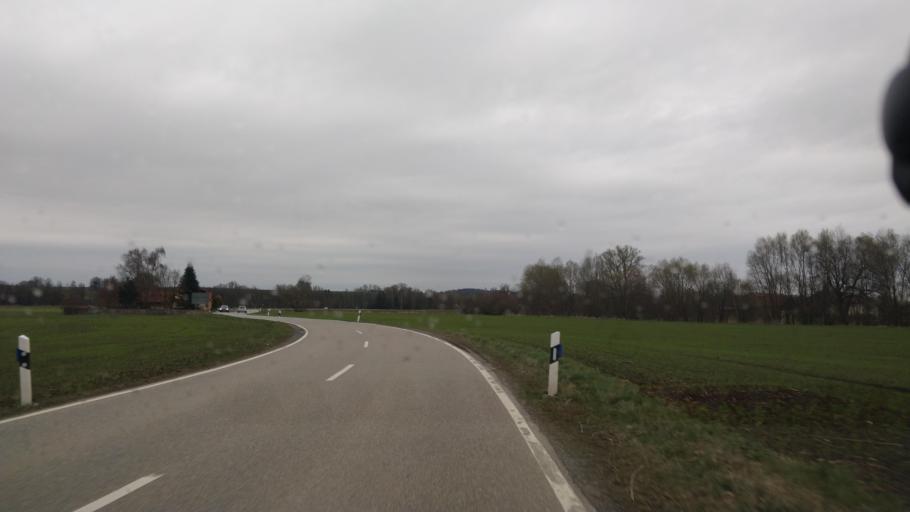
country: DE
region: Bavaria
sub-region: Upper Bavaria
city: Schwindegg
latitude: 48.2761
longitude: 12.2603
